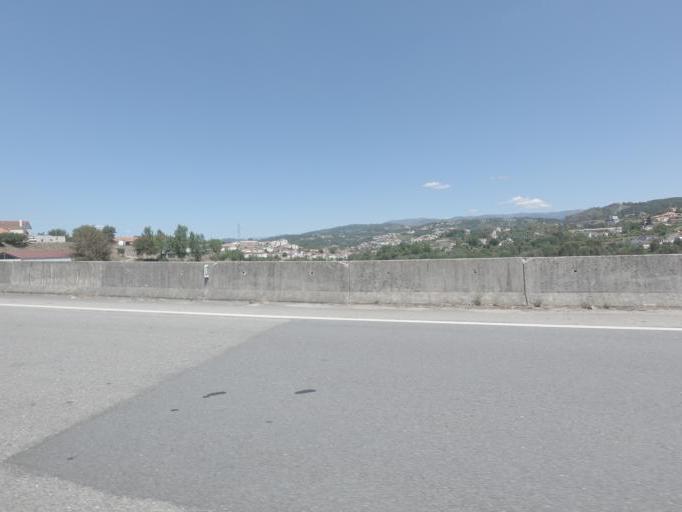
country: PT
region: Porto
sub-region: Amarante
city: Amarante
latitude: 41.2653
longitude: -8.0917
